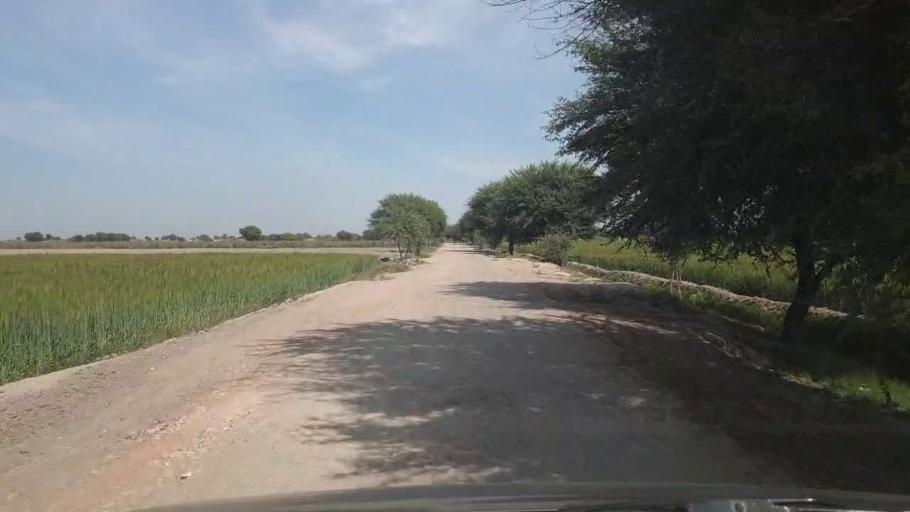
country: PK
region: Sindh
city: Kunri
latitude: 25.2220
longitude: 69.6519
